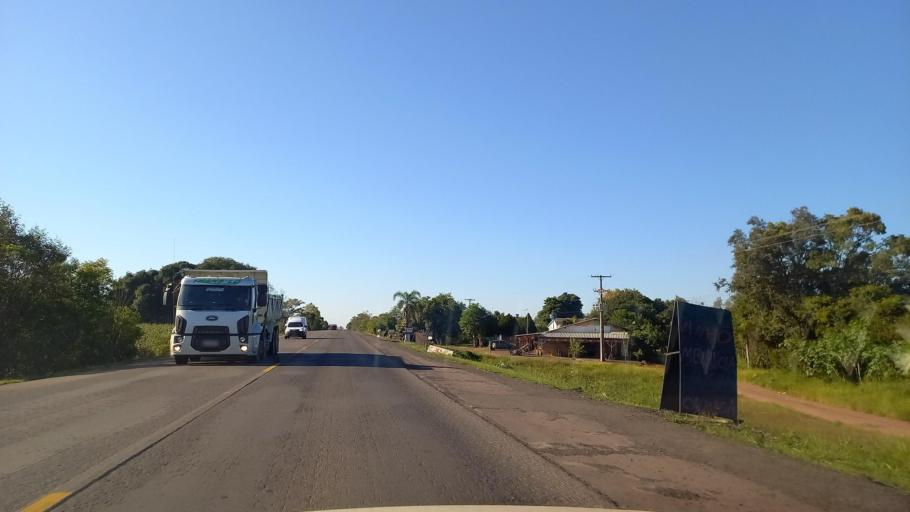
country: BR
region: Rio Grande do Sul
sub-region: Venancio Aires
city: Venancio Aires
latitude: -29.6709
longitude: -52.0233
